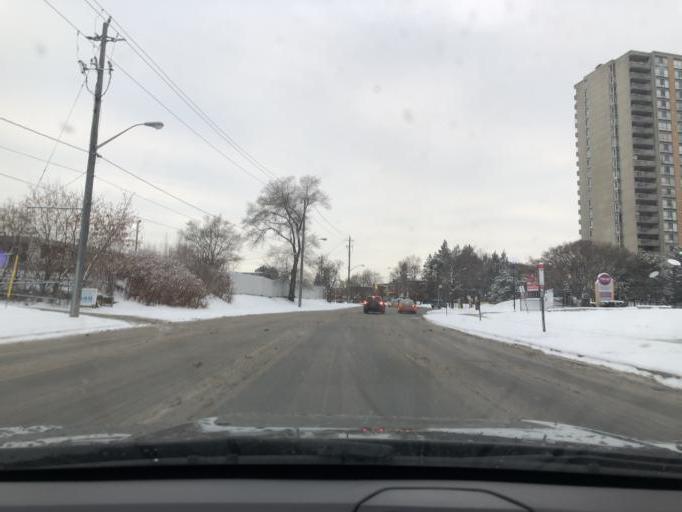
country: CA
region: Ontario
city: Toronto
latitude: 43.6959
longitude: -79.4890
